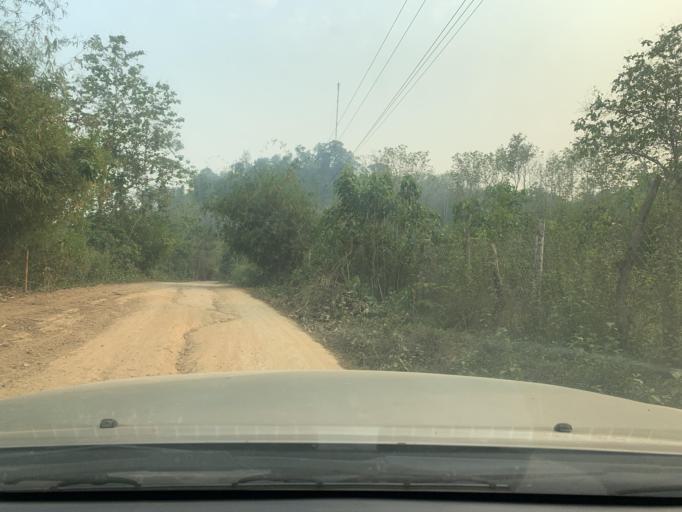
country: LA
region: Louangphabang
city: Louangphabang
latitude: 19.9247
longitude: 102.0743
